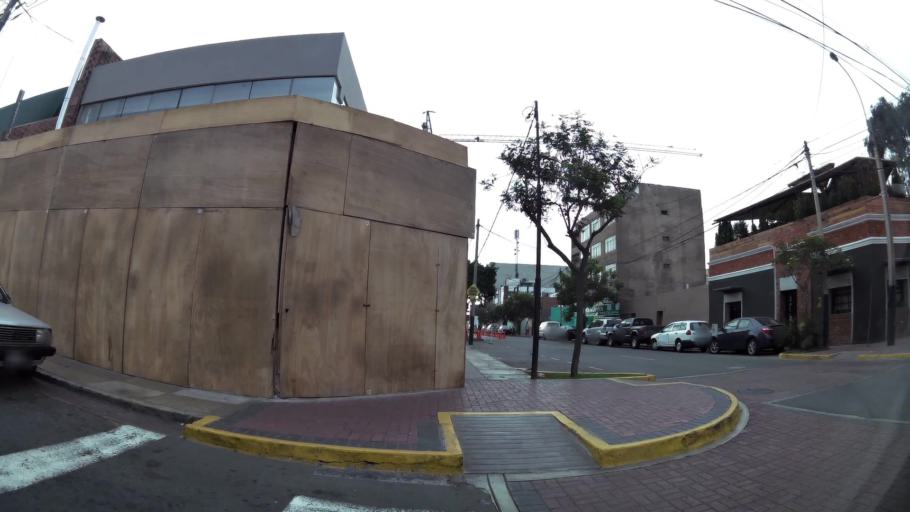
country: PE
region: Lima
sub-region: Lima
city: San Isidro
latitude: -12.1104
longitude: -77.0486
